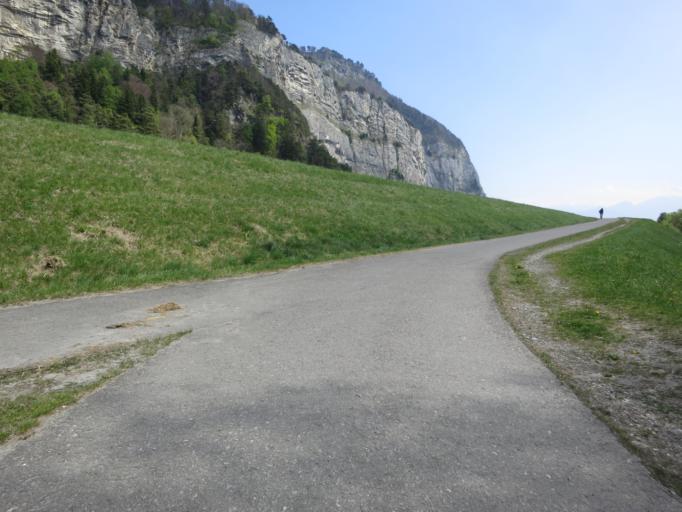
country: LI
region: Balzers
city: Balzers
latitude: 47.0484
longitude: 9.4763
